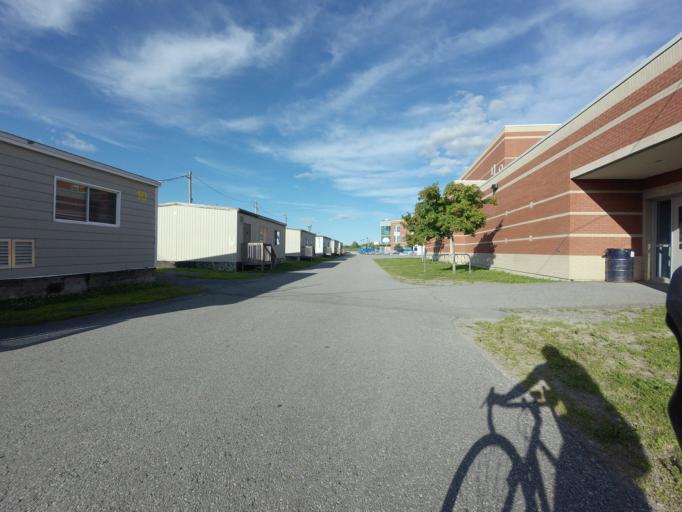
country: CA
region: Ontario
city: Ottawa
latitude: 45.2909
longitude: -75.6701
